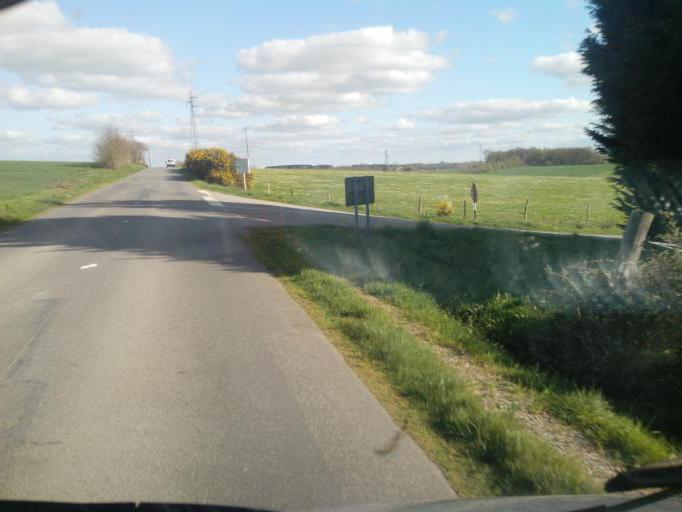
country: FR
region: Brittany
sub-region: Departement d'Ille-et-Vilaine
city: Grand-Fougeray
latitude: 47.7693
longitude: -1.7576
